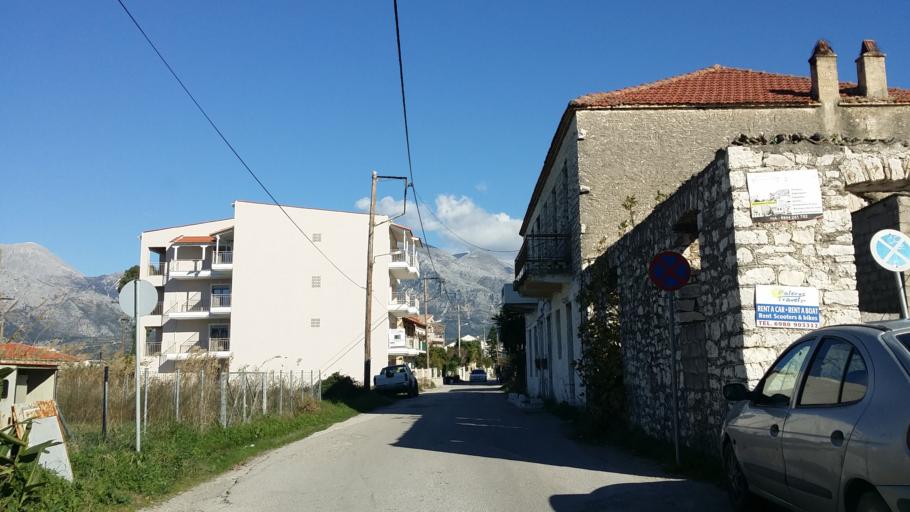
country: GR
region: West Greece
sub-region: Nomos Aitolias kai Akarnanias
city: Kandila
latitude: 38.6684
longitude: 20.9473
